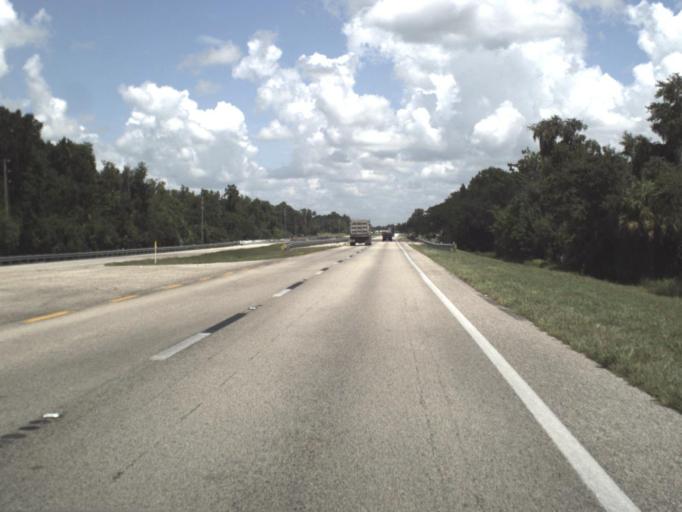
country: US
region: Florida
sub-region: Polk County
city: Fort Meade
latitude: 27.7048
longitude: -81.8081
